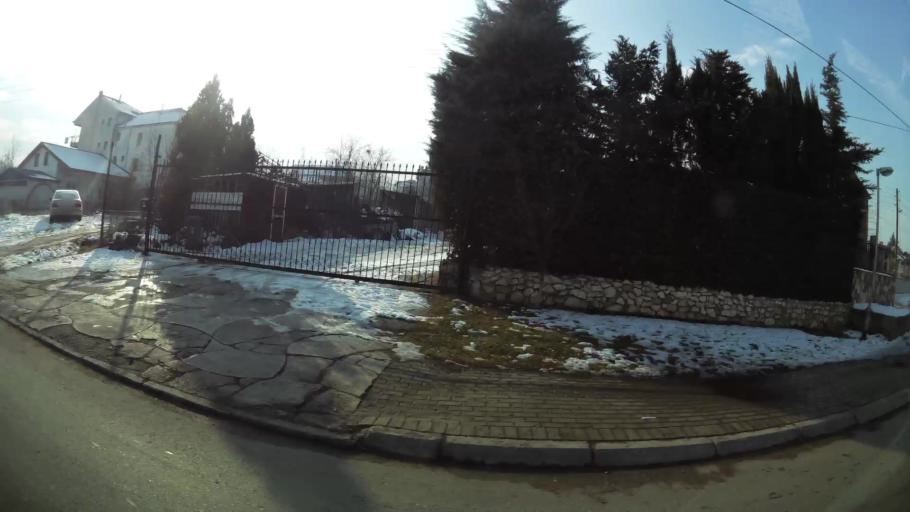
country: MK
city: Creshevo
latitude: 42.0095
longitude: 21.5015
